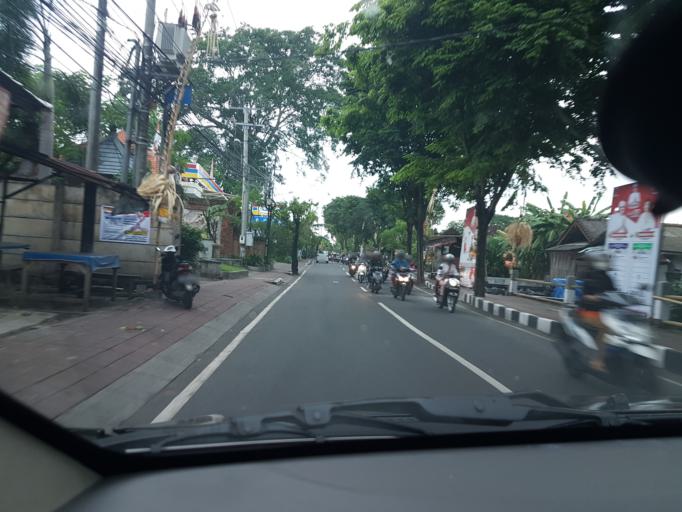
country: ID
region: Bali
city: Banjar Gunungpande
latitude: -8.6490
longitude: 115.1699
